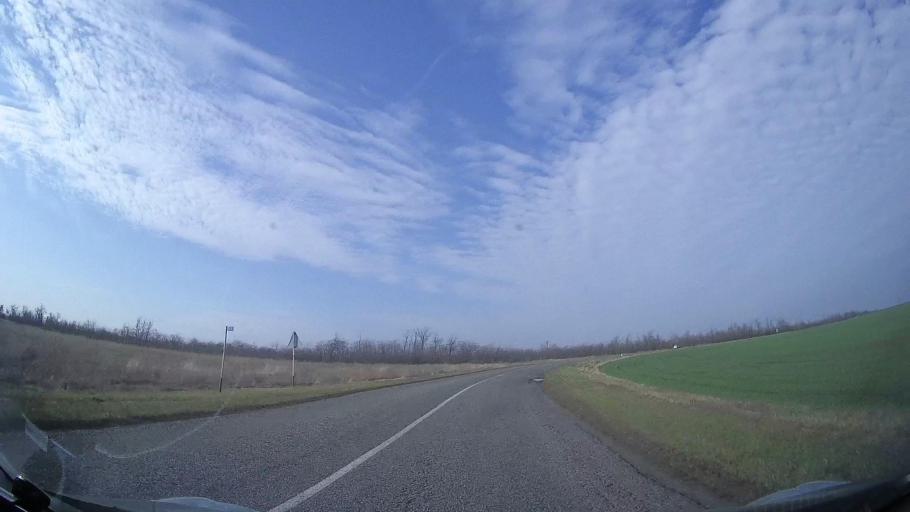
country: RU
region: Rostov
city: Gigant
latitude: 46.8448
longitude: 41.2897
